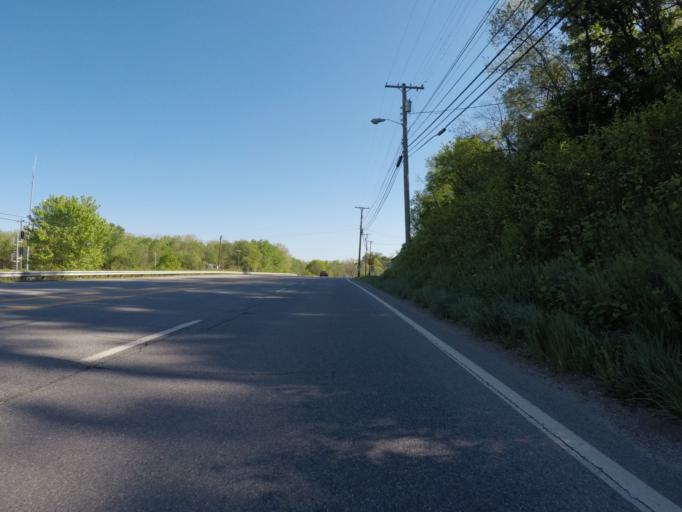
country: US
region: Kentucky
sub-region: Boyd County
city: Catlettsburg
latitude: 38.3993
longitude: -82.6010
